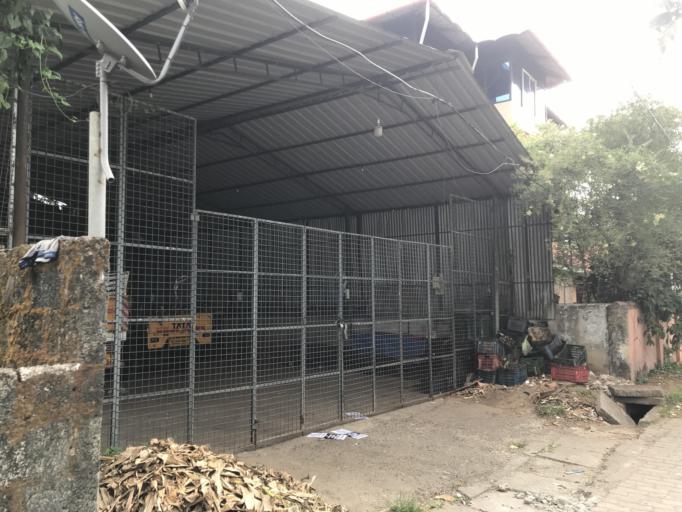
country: IN
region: Kerala
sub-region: Ernakulam
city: Aluva
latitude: 10.1058
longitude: 76.3485
